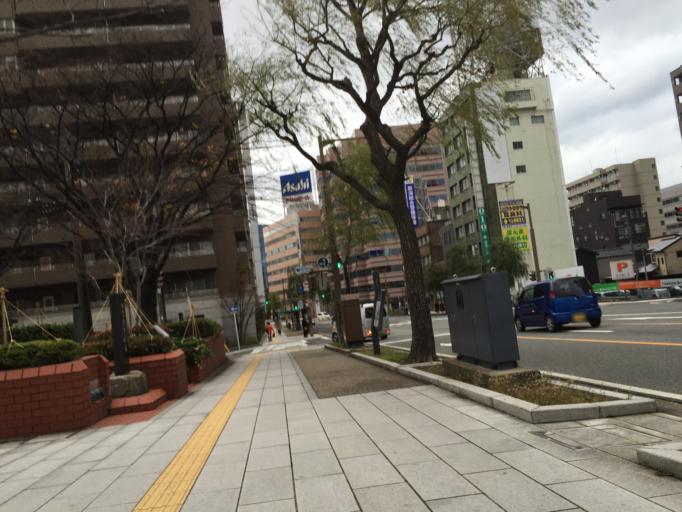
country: JP
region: Niigata
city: Niigata-shi
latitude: 37.9203
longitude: 139.0513
